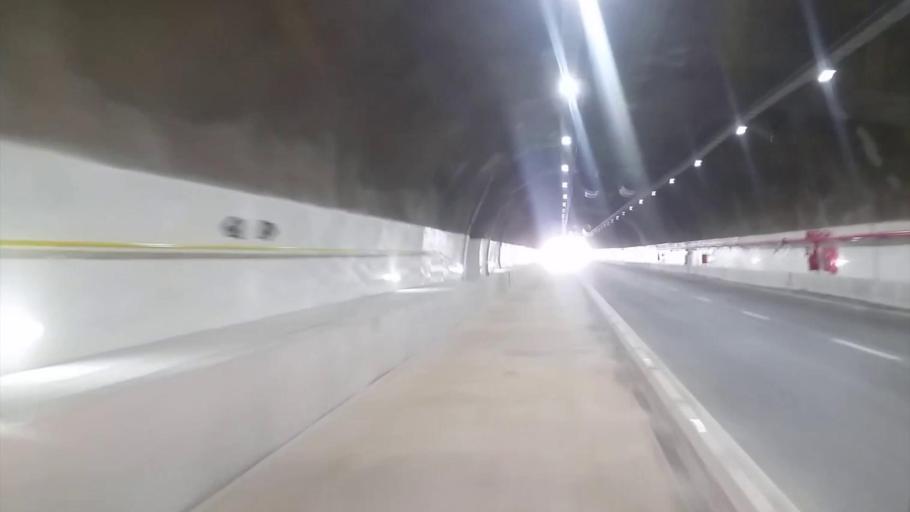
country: BR
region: Rio de Janeiro
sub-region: Nilopolis
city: Nilopolis
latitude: -22.8997
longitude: -43.3981
